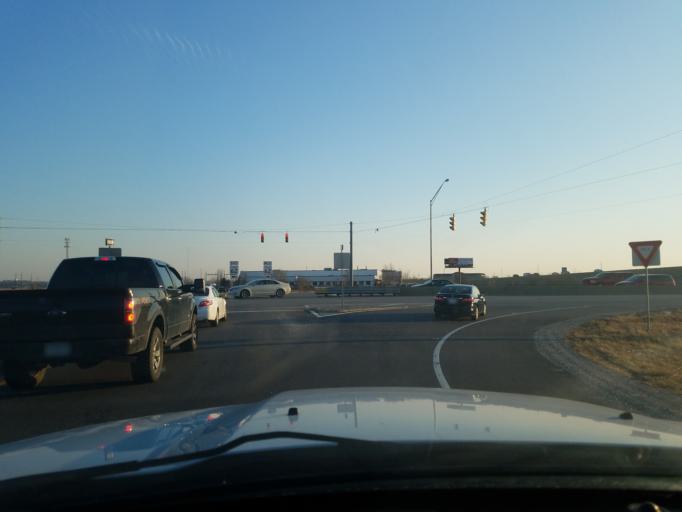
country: US
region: Indiana
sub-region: Vanderburgh County
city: Melody Hill
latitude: 37.9974
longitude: -87.4641
